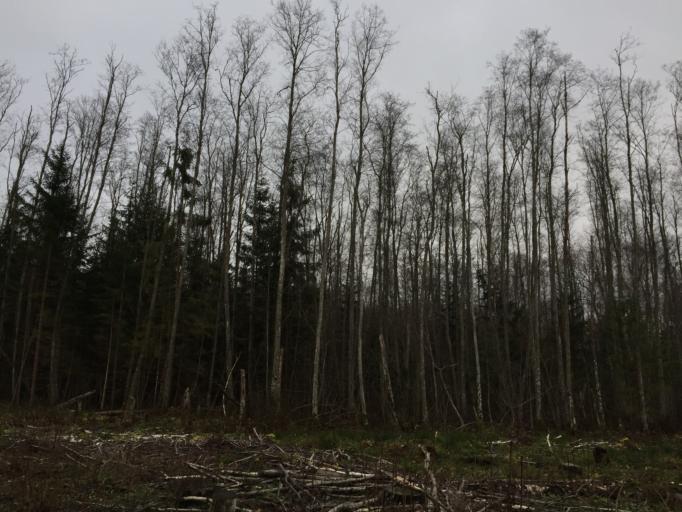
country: LV
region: Limbazu Rajons
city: Limbazi
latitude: 57.4197
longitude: 24.6321
